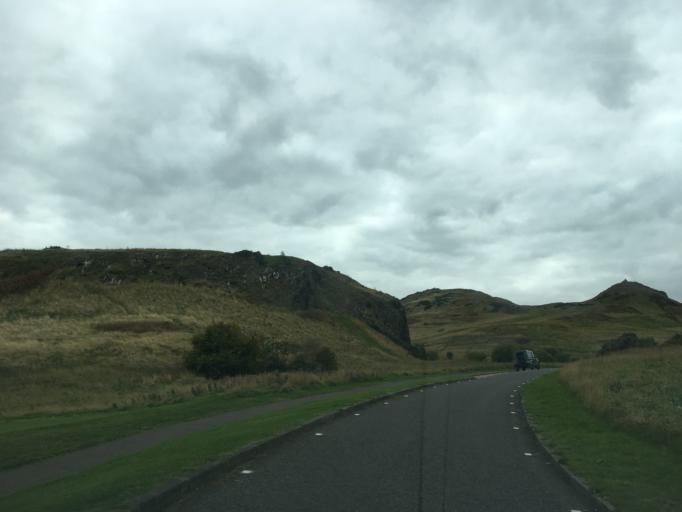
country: GB
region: Scotland
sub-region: West Lothian
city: Seafield
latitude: 55.9477
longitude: -3.1506
